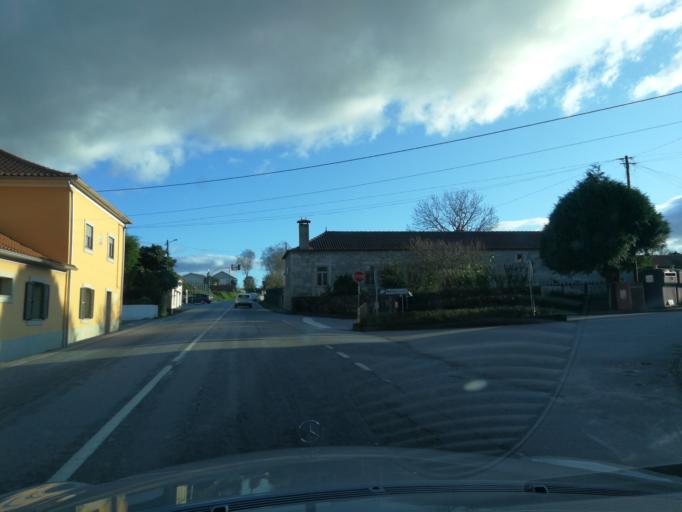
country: PT
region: Viana do Castelo
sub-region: Viana do Castelo
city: Darque
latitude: 41.6237
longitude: -8.7571
